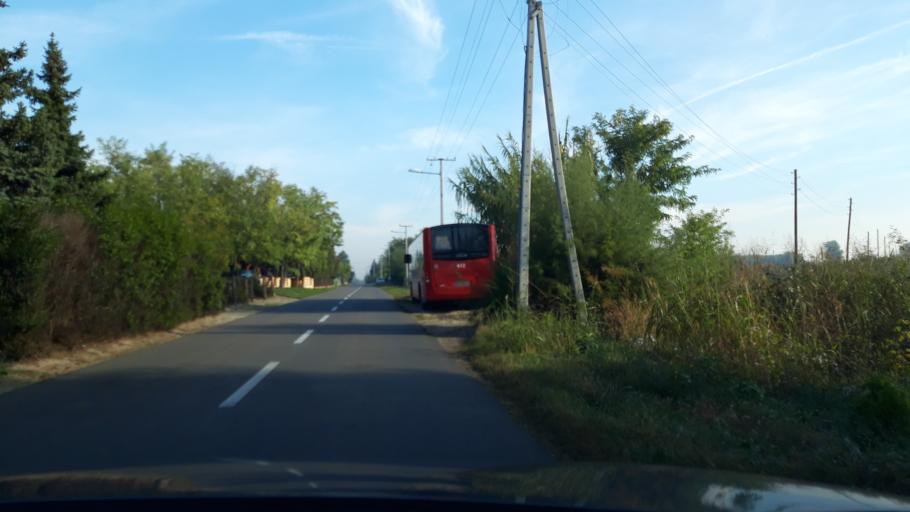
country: HU
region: Csongrad
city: Asotthalom
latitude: 46.1161
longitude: 19.8421
